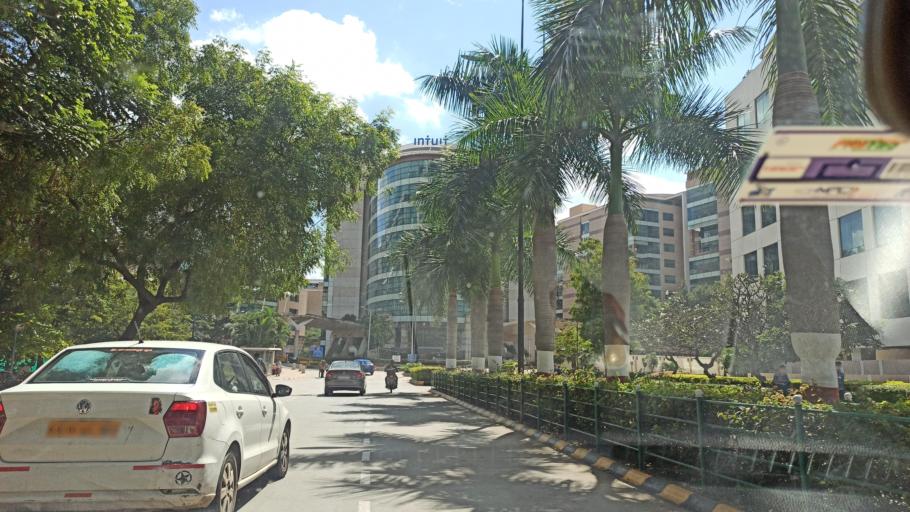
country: IN
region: Karnataka
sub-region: Bangalore Urban
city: Bangalore
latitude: 12.9251
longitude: 77.6814
